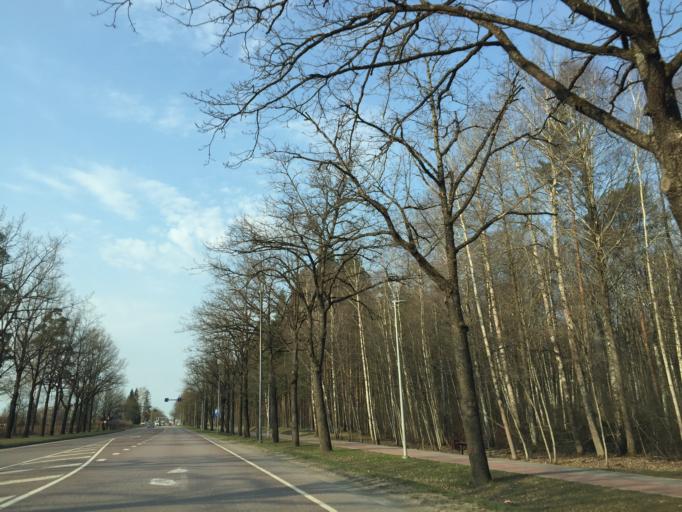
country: LV
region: Ozolnieku
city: Ozolnieki
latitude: 56.6757
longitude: 23.7713
